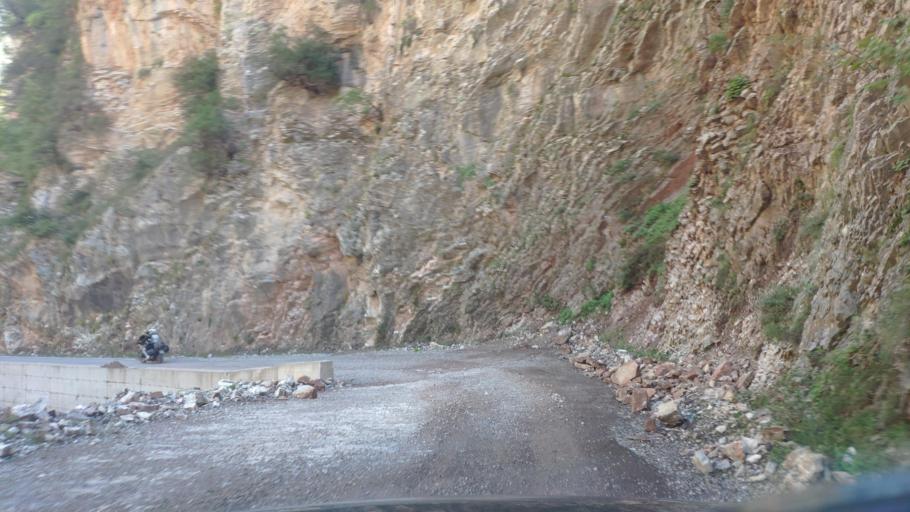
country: GR
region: Central Greece
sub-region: Nomos Evrytanias
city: Kerasochori
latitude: 39.1357
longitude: 21.6359
